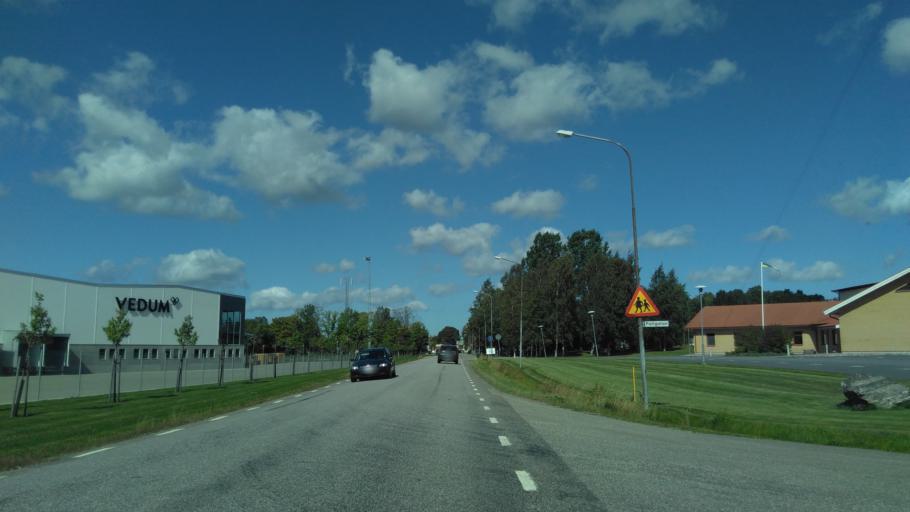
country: SE
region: Vaestra Goetaland
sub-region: Herrljunga Kommun
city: Herrljunga
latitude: 58.1665
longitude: 13.0024
